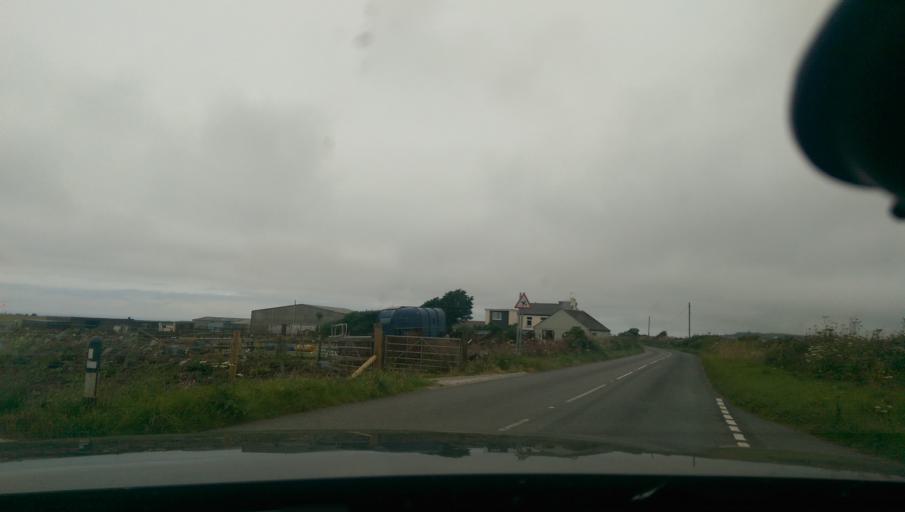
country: GB
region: England
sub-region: Cornwall
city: Saint Just
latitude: 50.1005
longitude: -5.6658
